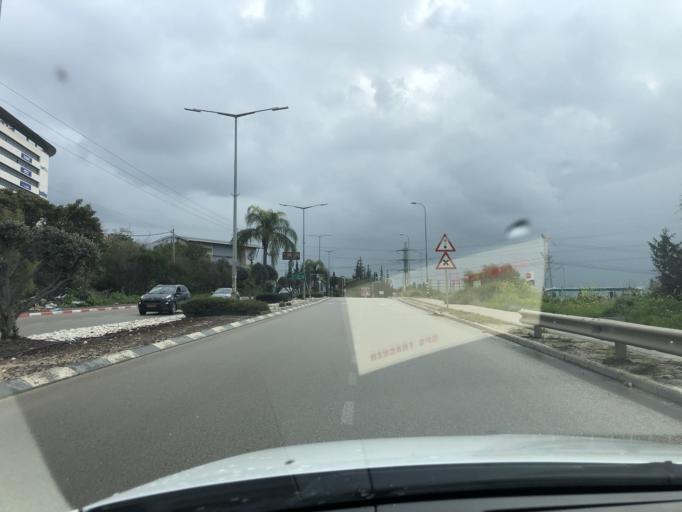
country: IL
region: Central District
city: Kafr Qasim
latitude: 32.1107
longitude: 34.9635
